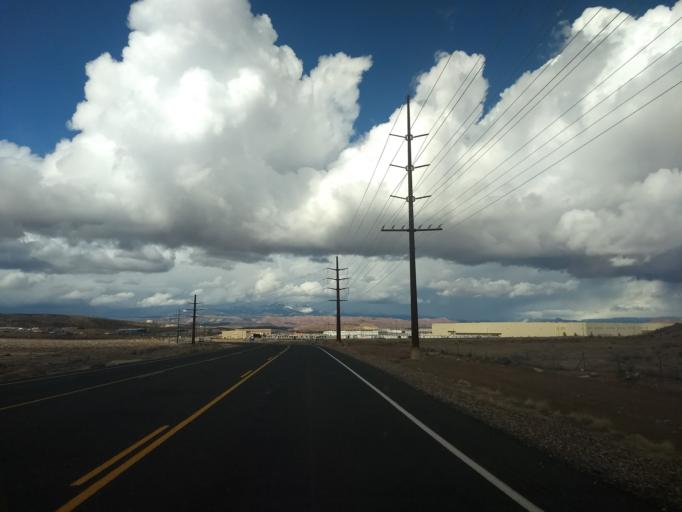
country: US
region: Utah
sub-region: Washington County
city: Saint George
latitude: 37.0209
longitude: -113.5634
